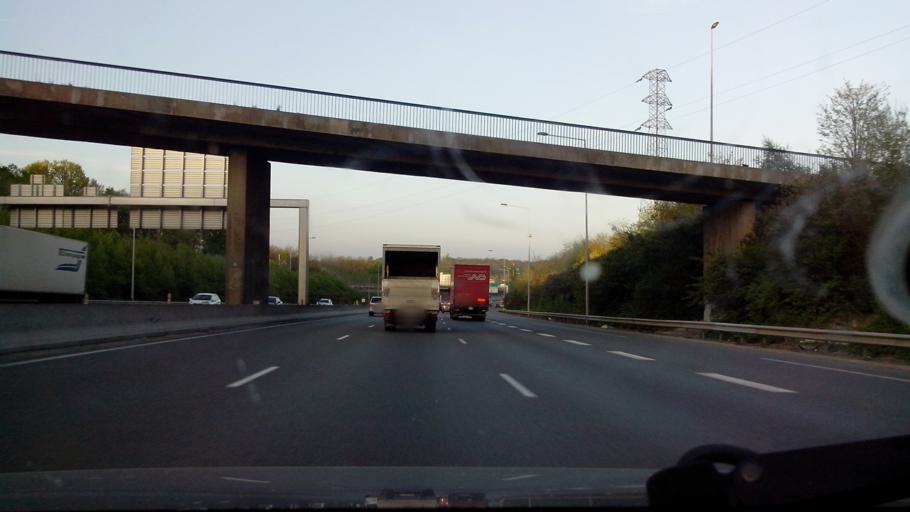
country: FR
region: Ile-de-France
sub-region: Departement de l'Essonne
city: Evry
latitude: 48.6204
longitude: 2.4607
